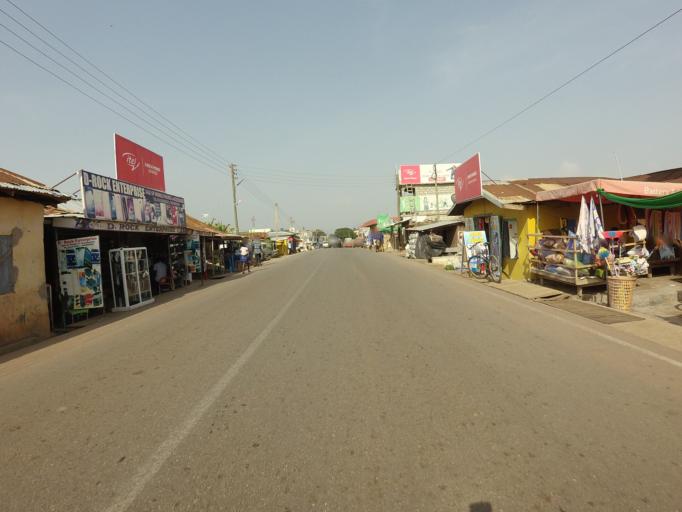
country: GH
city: Akropong
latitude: 6.1063
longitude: -0.0125
